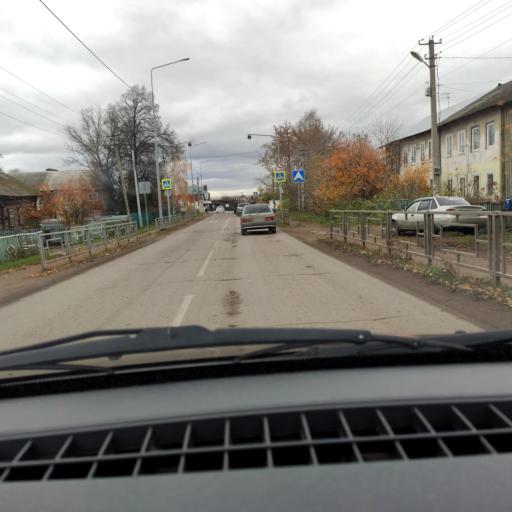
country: RU
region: Bashkortostan
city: Avdon
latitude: 54.4987
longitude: 55.8881
